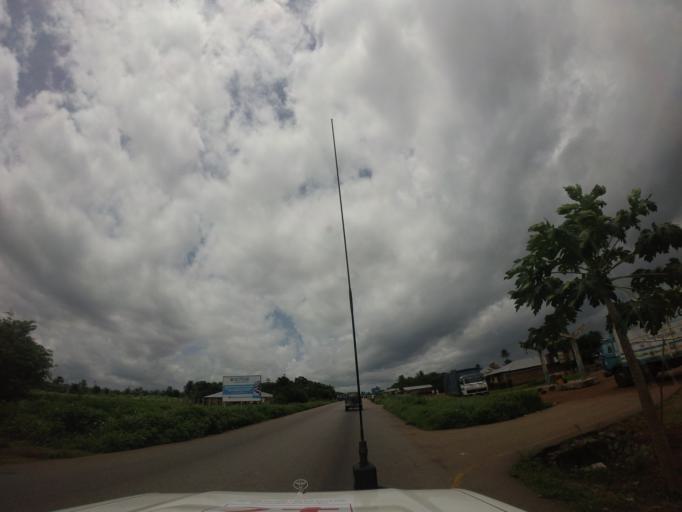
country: SL
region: Southern Province
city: Rotifunk
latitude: 8.4574
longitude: -12.6723
